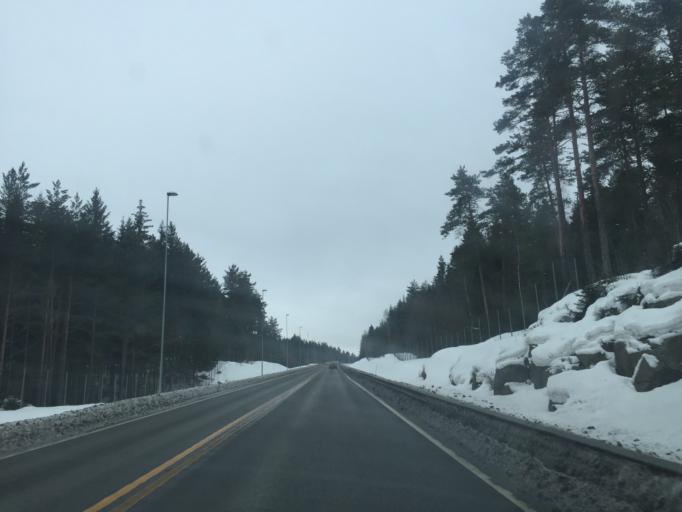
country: NO
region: Hedmark
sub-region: Loten
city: Loten
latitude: 60.7450
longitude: 11.3002
